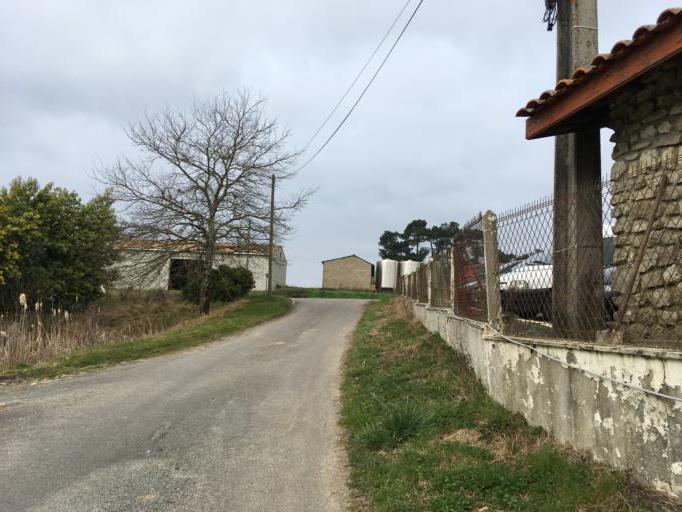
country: FR
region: Poitou-Charentes
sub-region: Departement de la Charente-Maritime
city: Mirambeau
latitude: 45.3345
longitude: -0.5932
